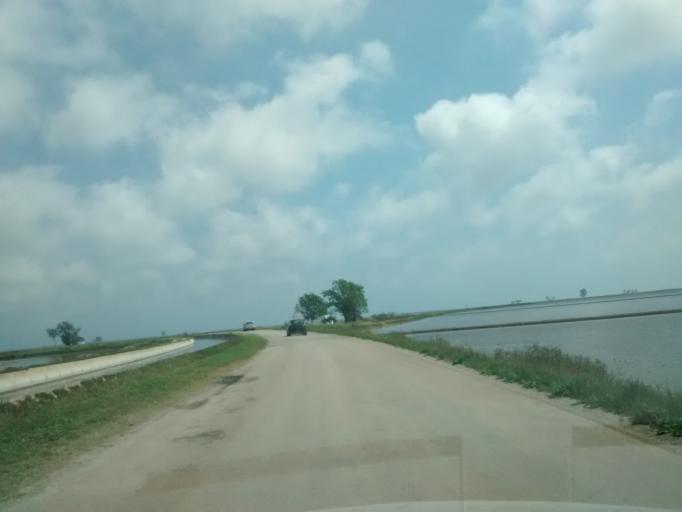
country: ES
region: Catalonia
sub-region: Provincia de Tarragona
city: Deltebre
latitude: 40.6904
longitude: 0.7816
